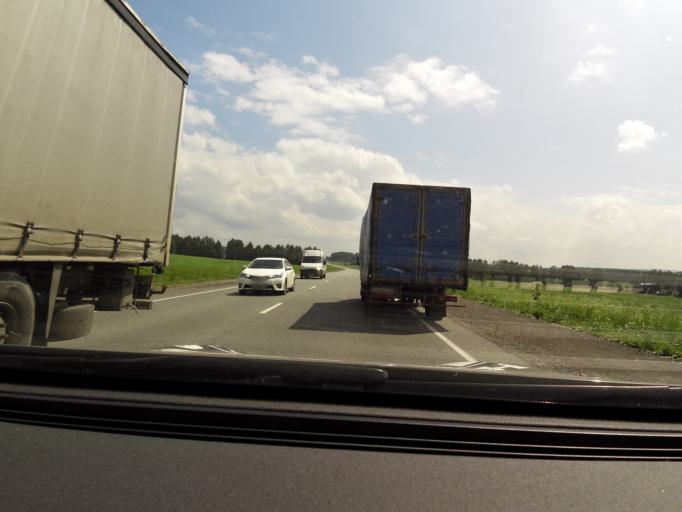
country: RU
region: Perm
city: Suksun
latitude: 57.0342
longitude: 57.4479
